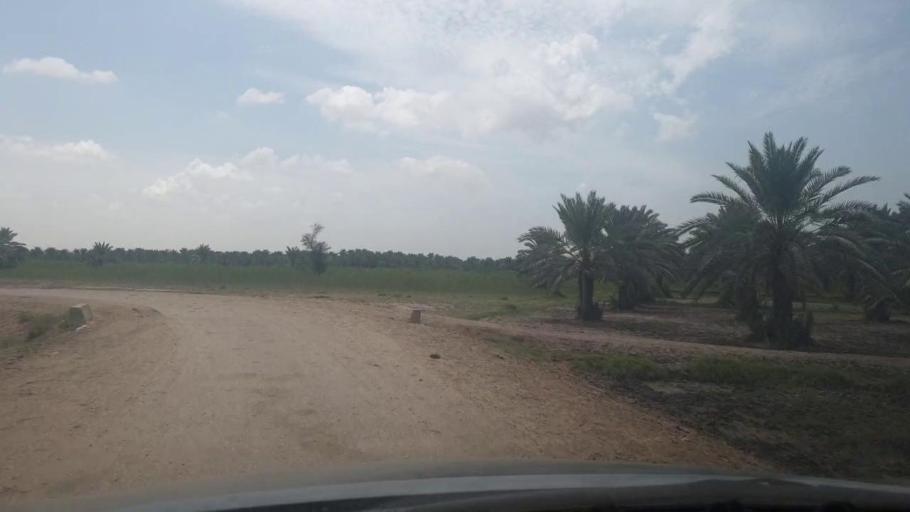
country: PK
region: Sindh
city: Kot Diji
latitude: 27.3930
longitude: 68.7623
